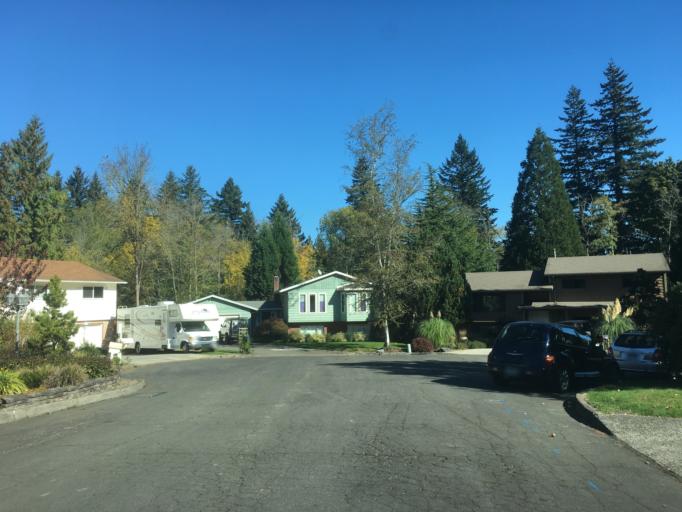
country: US
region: Oregon
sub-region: Multnomah County
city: Gresham
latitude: 45.4825
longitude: -122.4207
